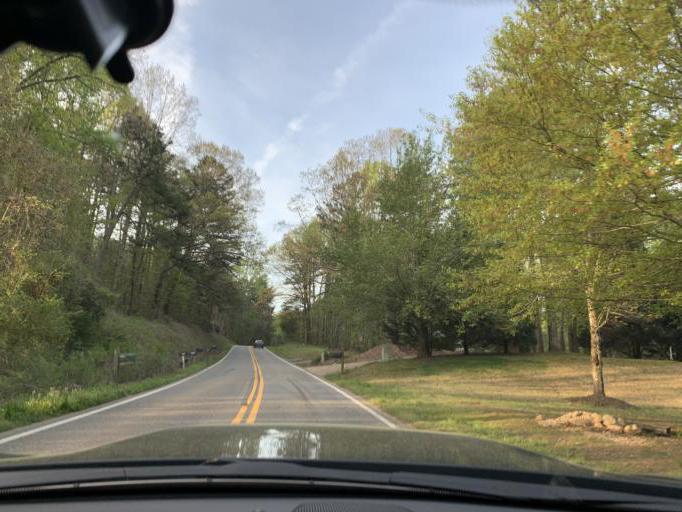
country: US
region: Georgia
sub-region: Forsyth County
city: Cumming
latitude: 34.2516
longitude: -84.1448
